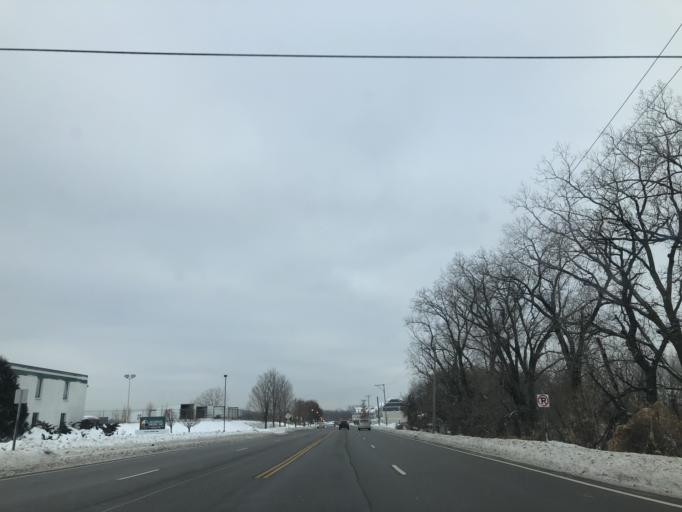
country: US
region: Minnesota
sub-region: Ramsey County
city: New Brighton
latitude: 45.0751
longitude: -93.1888
